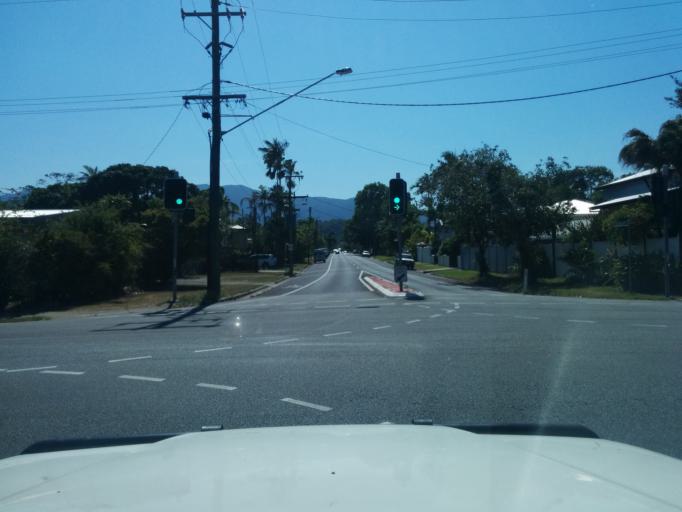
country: AU
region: Queensland
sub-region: Cairns
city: Cairns
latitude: -16.9031
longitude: 145.7421
